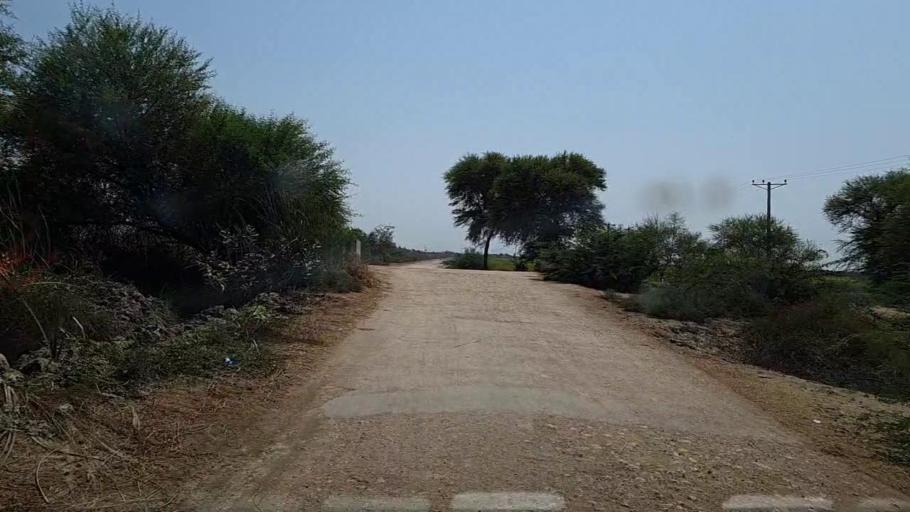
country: PK
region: Sindh
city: Mirpur Batoro
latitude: 24.6408
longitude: 68.4522
